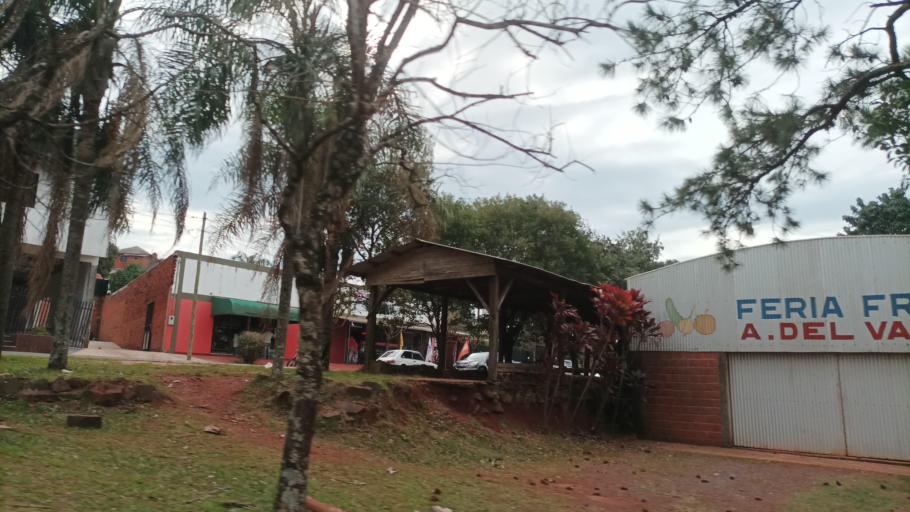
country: AR
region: Misiones
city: Aristobulo del Valle
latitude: -27.0946
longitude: -54.8914
